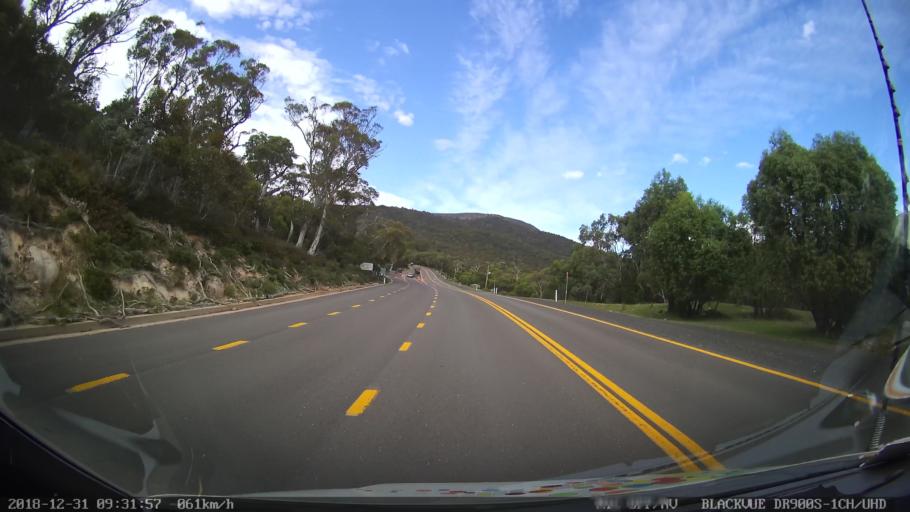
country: AU
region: New South Wales
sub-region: Snowy River
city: Jindabyne
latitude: -36.4497
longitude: 148.4386
